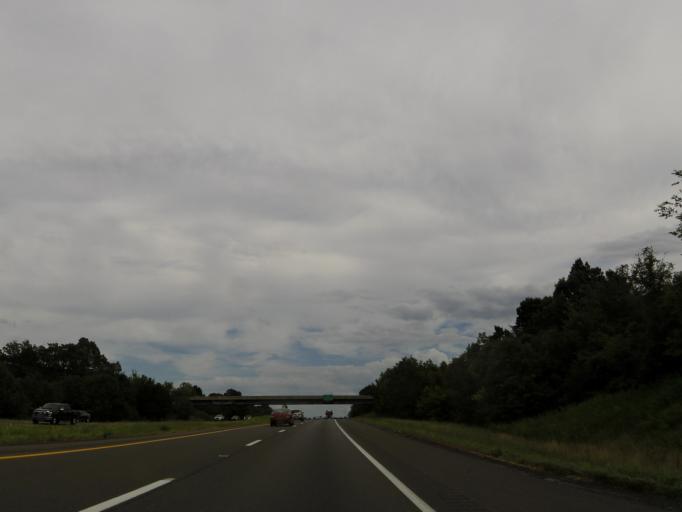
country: US
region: Kentucky
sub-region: Lyon County
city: Eddyville
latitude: 37.0639
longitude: -88.1953
